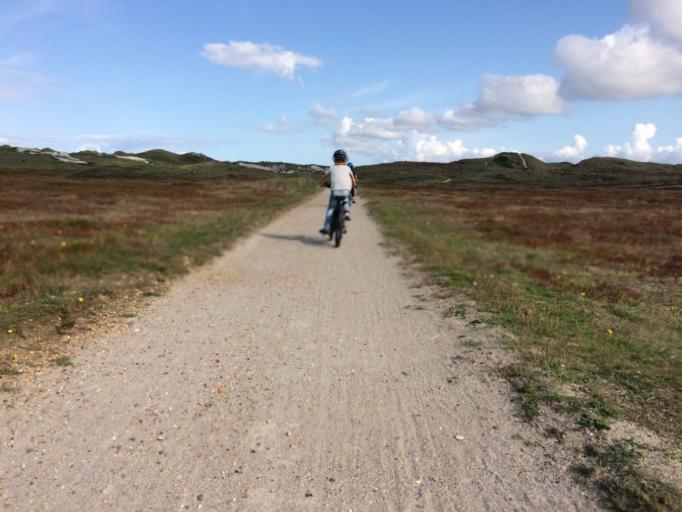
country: DK
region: Central Jutland
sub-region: Ringkobing-Skjern Kommune
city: Hvide Sande
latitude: 55.9081
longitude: 8.1563
